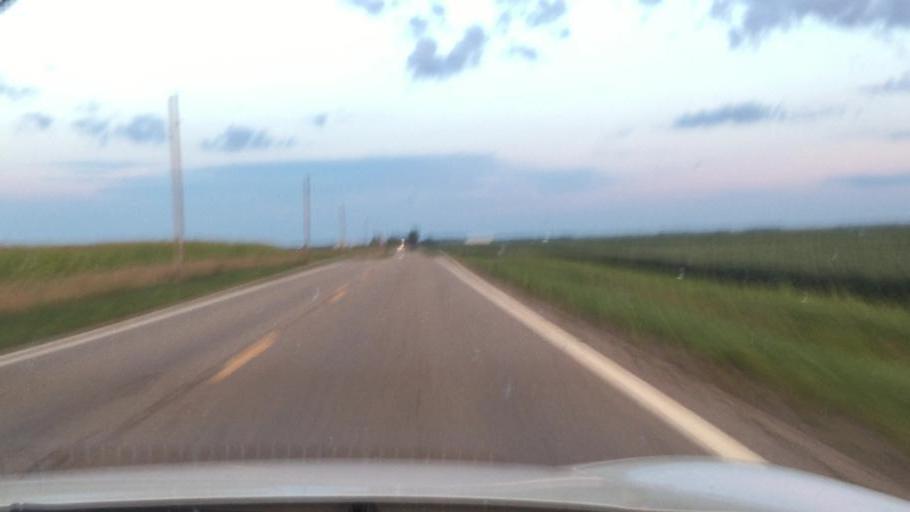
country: US
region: Ohio
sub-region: Madison County
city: Choctaw Lake
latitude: 40.0118
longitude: -83.4549
